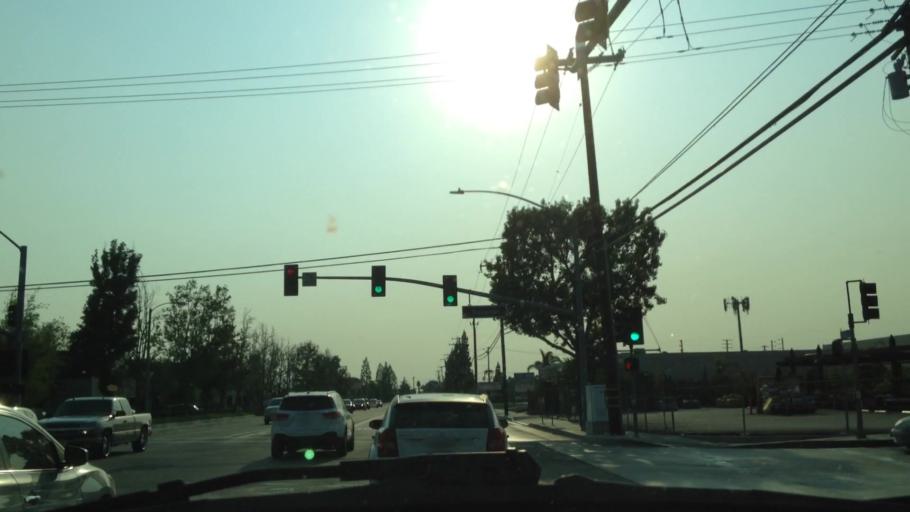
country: US
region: California
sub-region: Orange County
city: Orange
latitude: 33.8157
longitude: -117.8620
